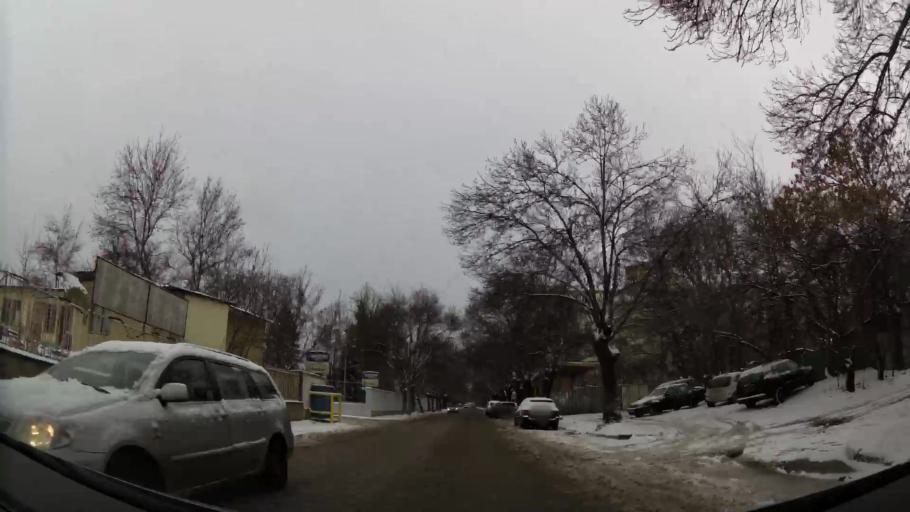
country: BG
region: Sofia-Capital
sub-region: Stolichna Obshtina
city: Sofia
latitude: 42.6942
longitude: 23.3007
